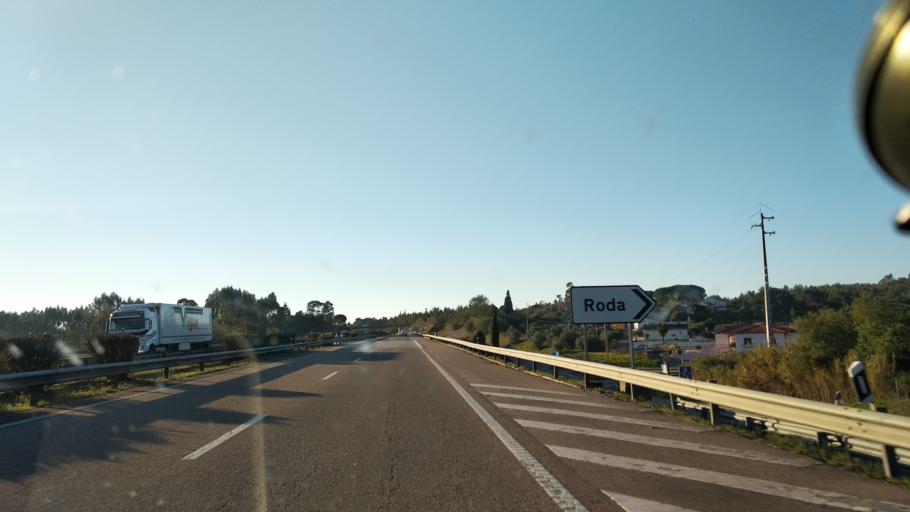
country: PT
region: Santarem
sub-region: Chamusca
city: Vila Nova da Barquinha
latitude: 39.4869
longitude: -8.3884
